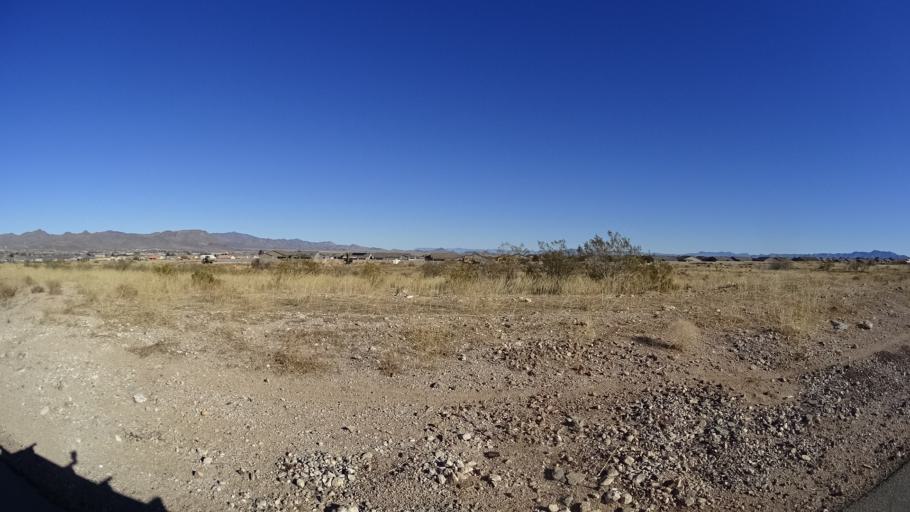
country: US
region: Arizona
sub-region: Mohave County
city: Kingman
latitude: 35.1884
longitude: -114.0011
